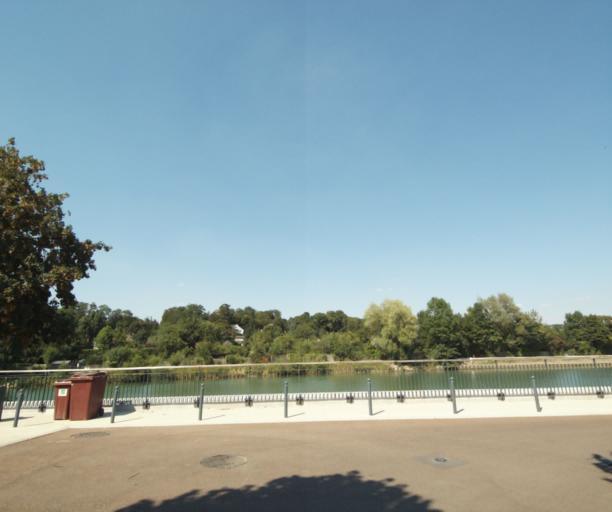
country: FR
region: Ile-de-France
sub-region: Departement de Seine-et-Marne
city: Pomponne
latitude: 48.8798
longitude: 2.6913
